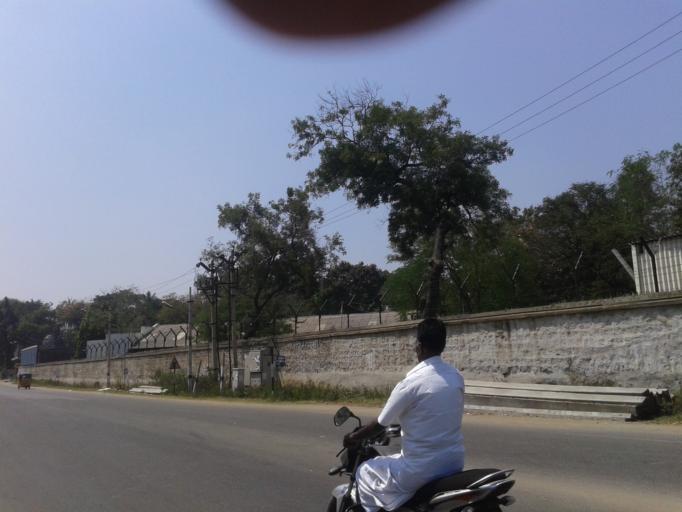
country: IN
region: Tamil Nadu
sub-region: Madurai
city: Madurai
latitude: 9.9342
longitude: 78.0896
